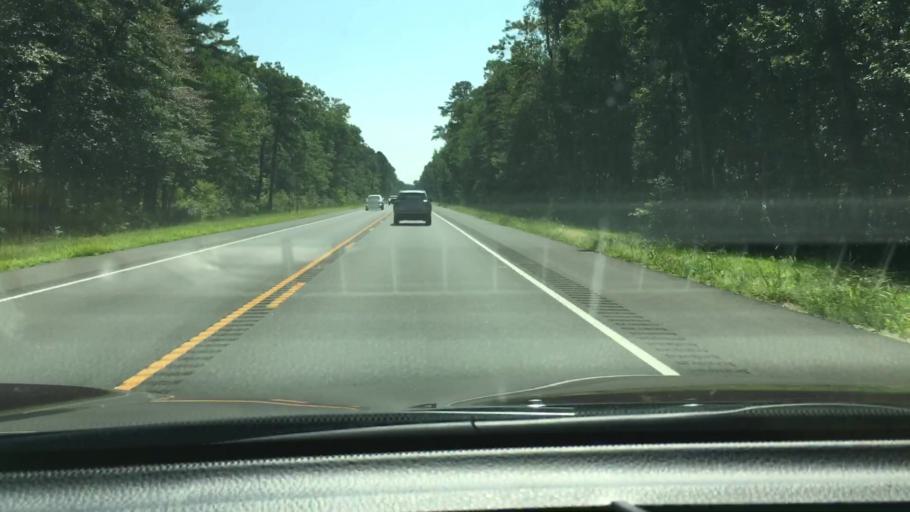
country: US
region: New Jersey
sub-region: Cape May County
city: Woodbine
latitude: 39.3156
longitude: -74.8335
